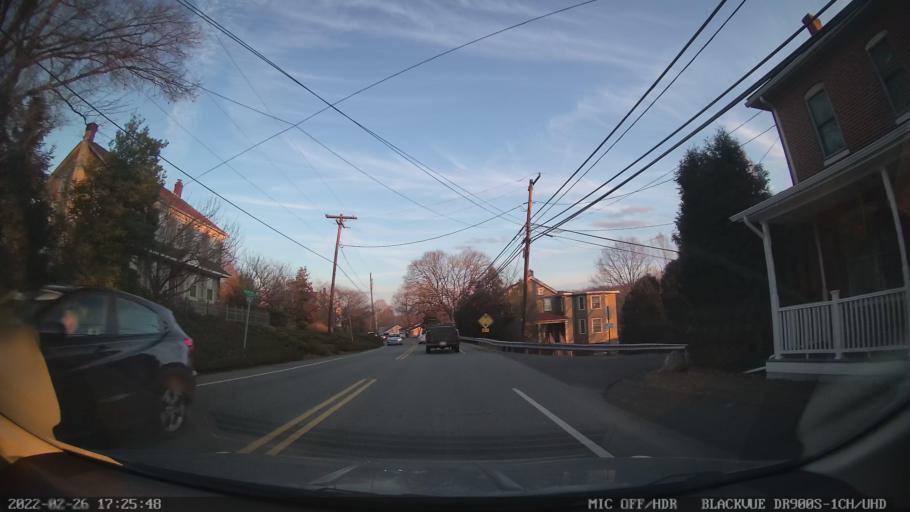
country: US
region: Pennsylvania
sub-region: Montgomery County
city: East Greenville
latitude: 40.4267
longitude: -75.5326
